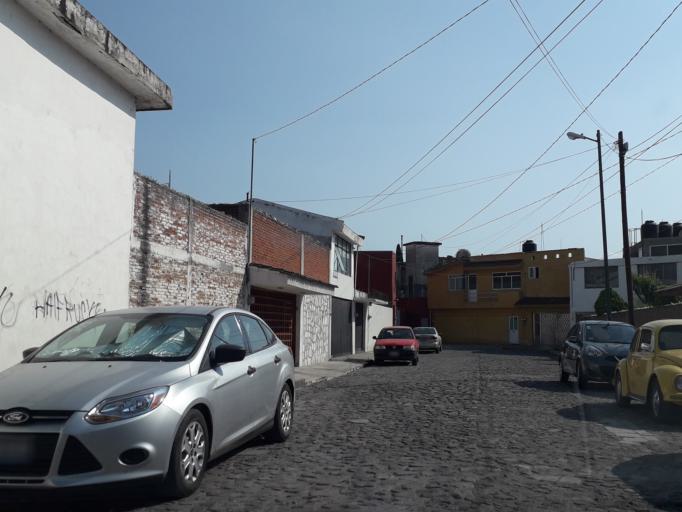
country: MX
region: Puebla
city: Puebla
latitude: 19.0153
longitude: -98.2124
